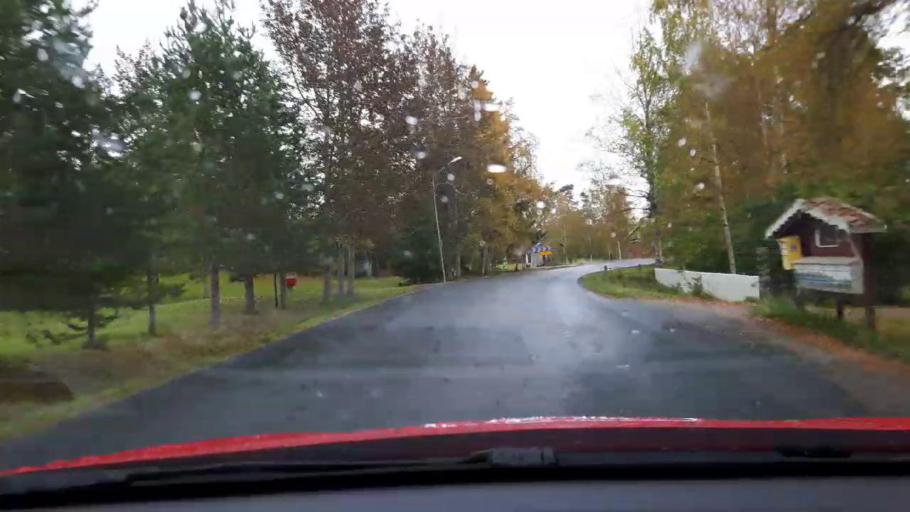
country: SE
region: Jaemtland
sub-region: Bergs Kommun
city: Hoverberg
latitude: 62.9368
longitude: 14.5113
